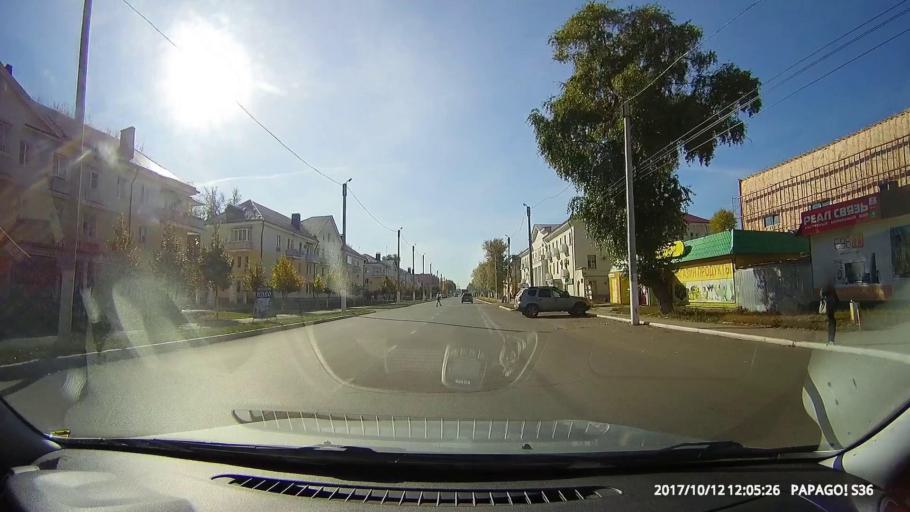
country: RU
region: Samara
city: Chapayevsk
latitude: 52.9771
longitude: 49.7120
